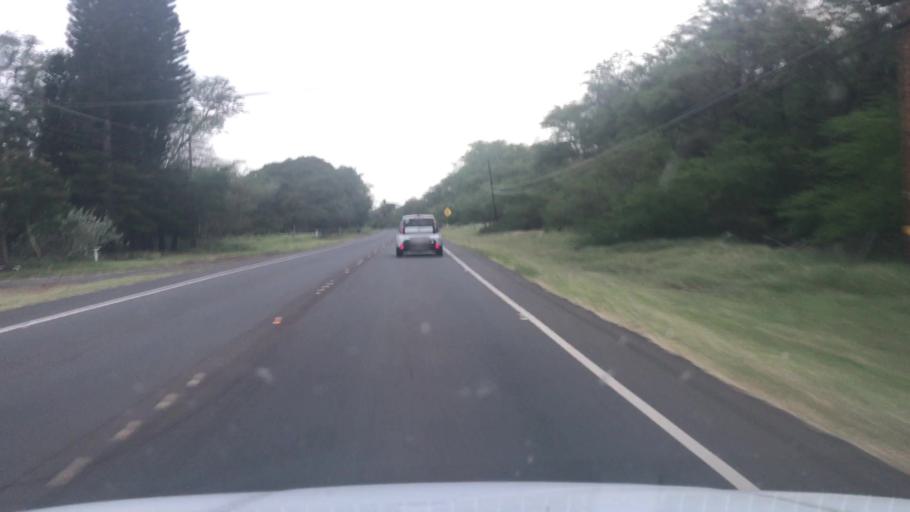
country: US
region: Hawaii
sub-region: Maui County
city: Kaunakakai
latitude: 21.0677
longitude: -156.9583
